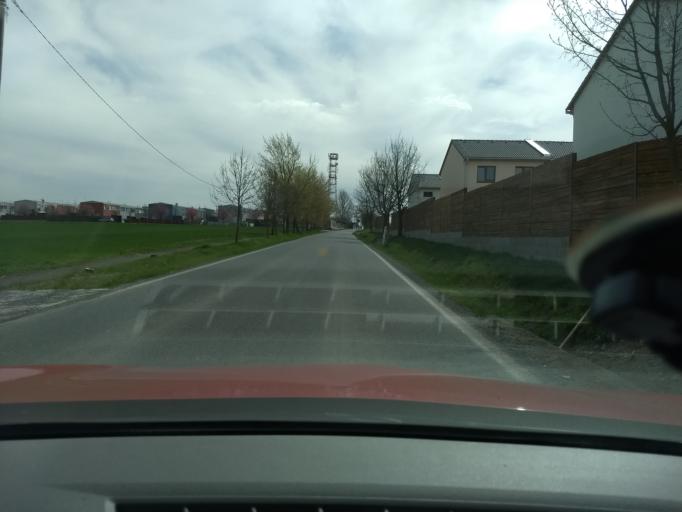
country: CZ
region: Central Bohemia
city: Rudna
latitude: 50.0547
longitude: 14.2260
